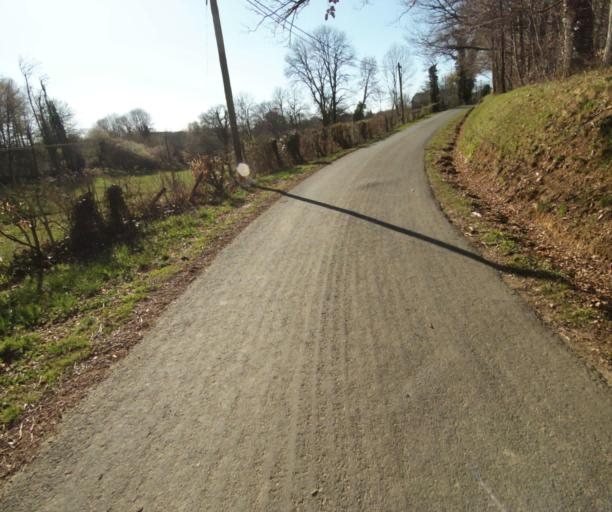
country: FR
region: Limousin
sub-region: Departement de la Correze
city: Chamboulive
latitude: 45.3929
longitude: 1.6699
